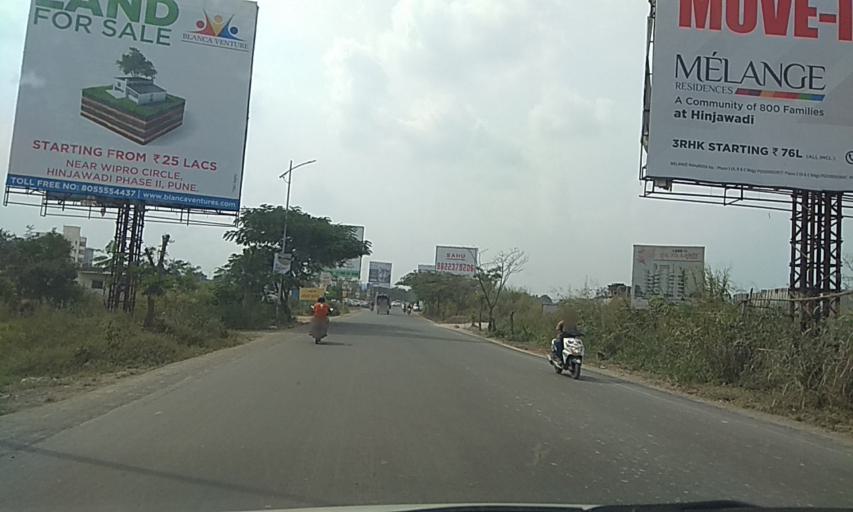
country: IN
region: Maharashtra
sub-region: Pune Division
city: Pimpri
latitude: 18.5814
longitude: 73.7241
